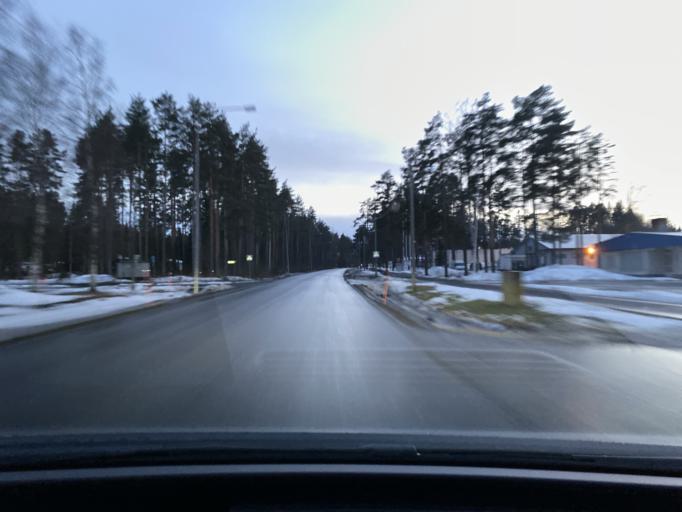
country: FI
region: Varsinais-Suomi
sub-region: Loimaa
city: Loimaa
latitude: 60.8501
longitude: 23.0378
